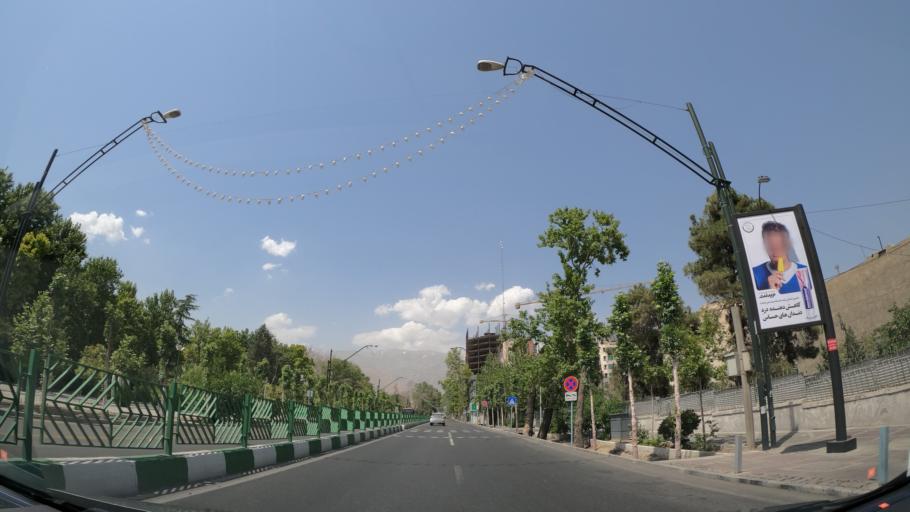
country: IR
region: Tehran
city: Tajrish
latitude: 35.7733
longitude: 51.4124
